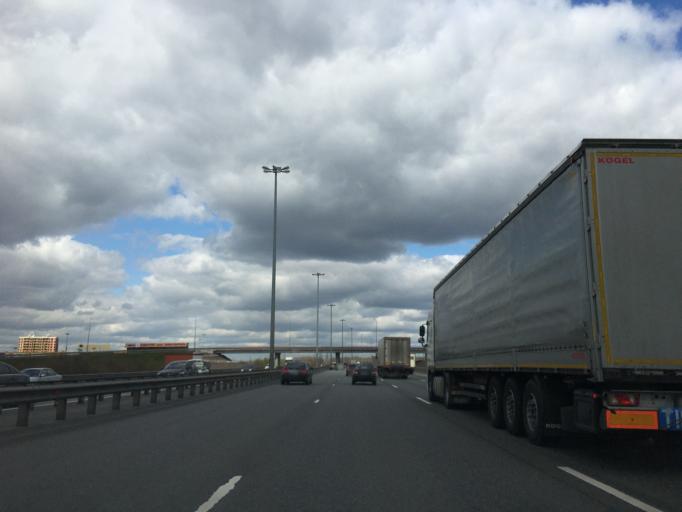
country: RU
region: St.-Petersburg
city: Krasnogvargeisky
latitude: 59.9139
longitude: 30.5259
